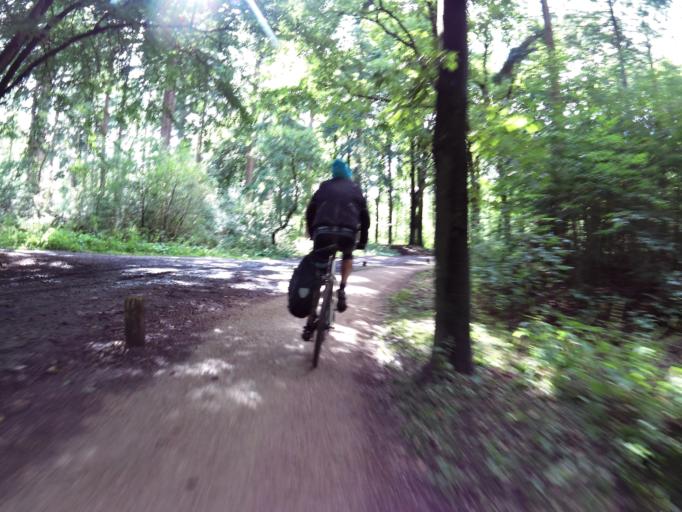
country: NL
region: North Holland
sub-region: Gemeente Hilversum
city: Hilversum
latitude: 52.1739
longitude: 5.2079
